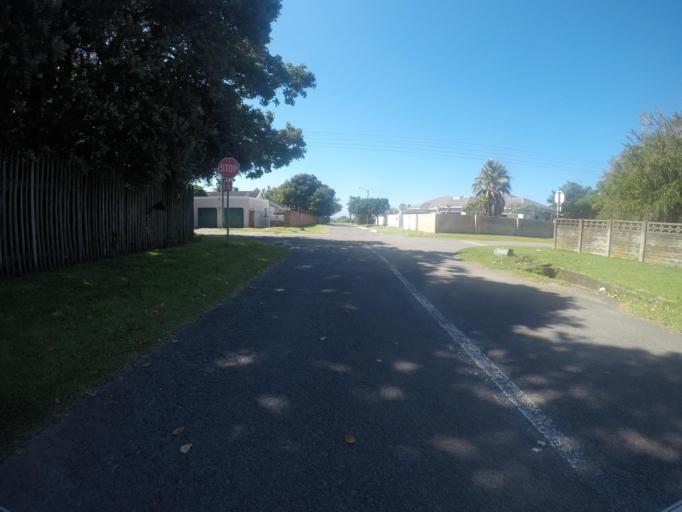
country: ZA
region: Eastern Cape
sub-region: Buffalo City Metropolitan Municipality
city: East London
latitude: -32.9475
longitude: 28.0082
